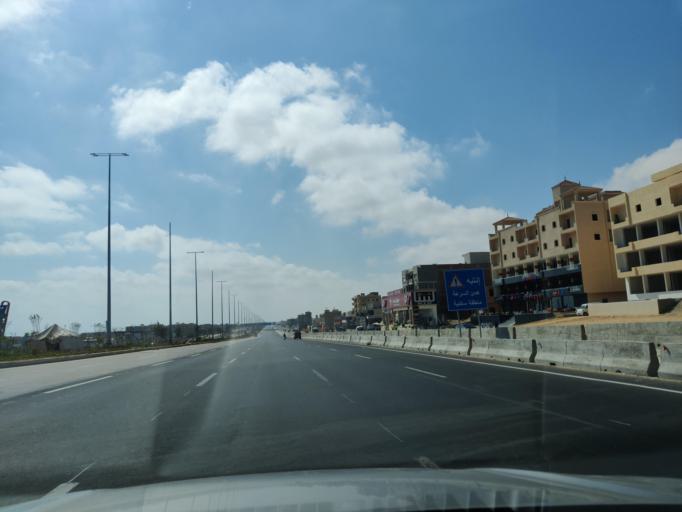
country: EG
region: Muhafazat Matruh
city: Al `Alamayn
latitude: 30.9736
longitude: 28.7339
